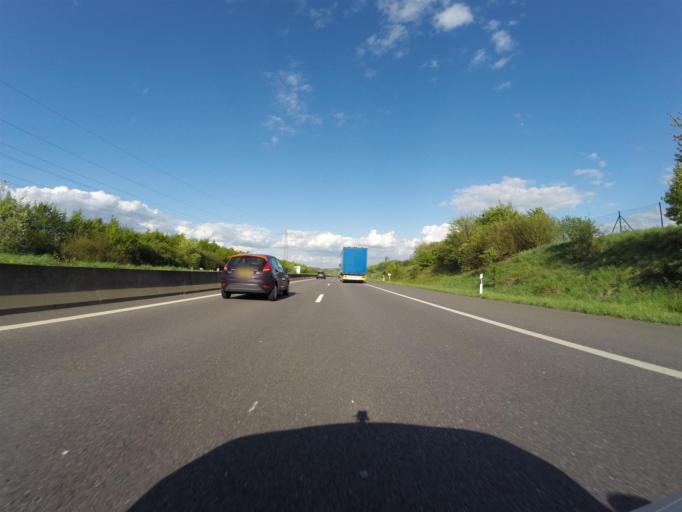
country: LU
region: Luxembourg
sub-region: Canton d'Esch-sur-Alzette
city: Frisange
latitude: 49.5093
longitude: 6.2074
